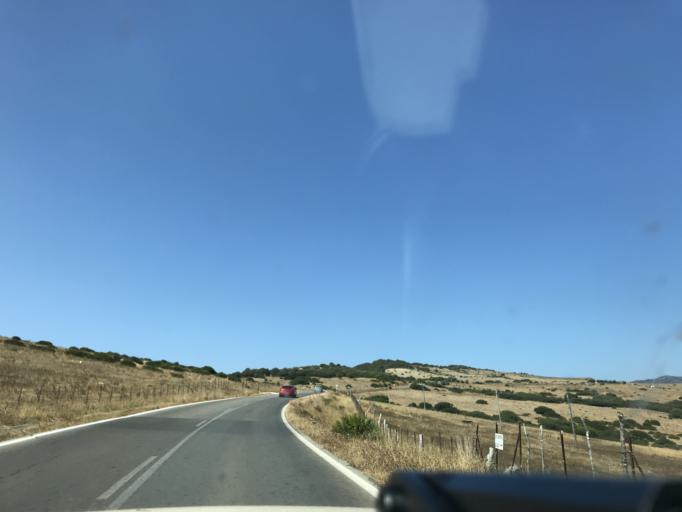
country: ES
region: Andalusia
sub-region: Provincia de Cadiz
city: Zahara de los Atunes
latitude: 36.0983
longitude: -5.7486
